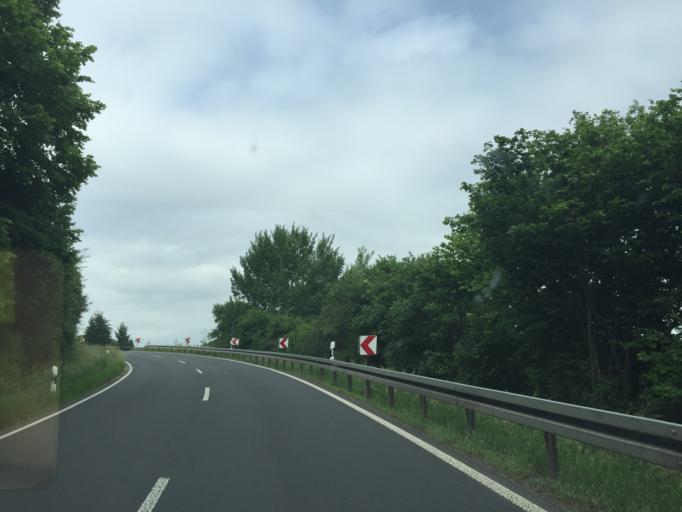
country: DE
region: Thuringia
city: Konigsee
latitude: 50.6620
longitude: 11.0795
